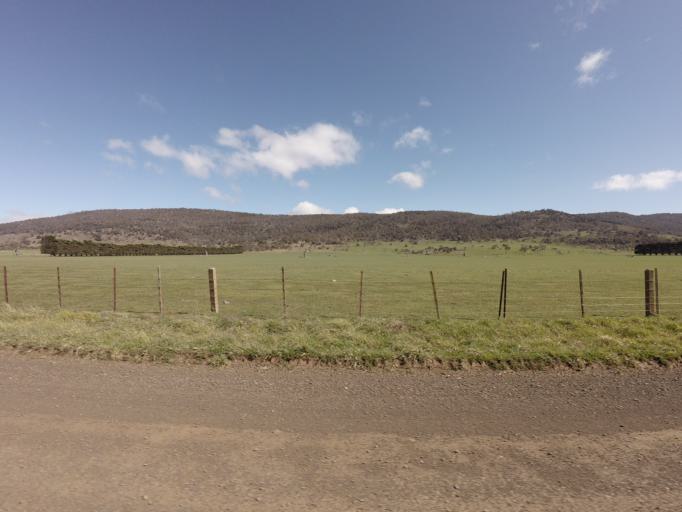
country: AU
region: Tasmania
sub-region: Northern Midlands
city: Evandale
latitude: -41.9604
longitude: 147.4383
